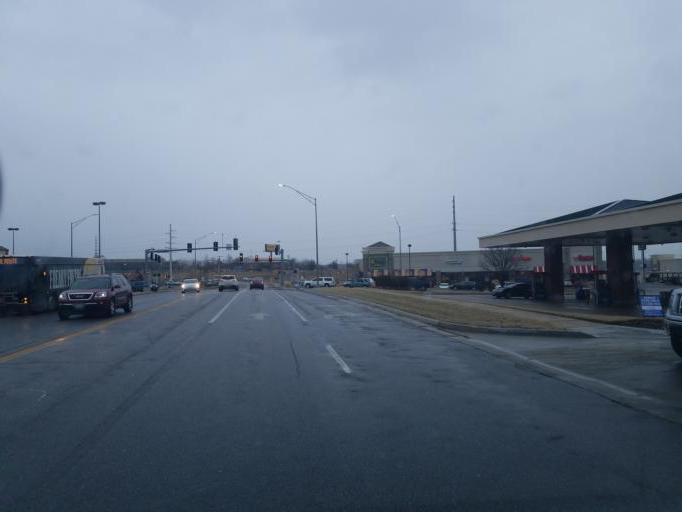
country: US
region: Missouri
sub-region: Boone County
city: Columbia
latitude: 38.9483
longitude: -92.2968
